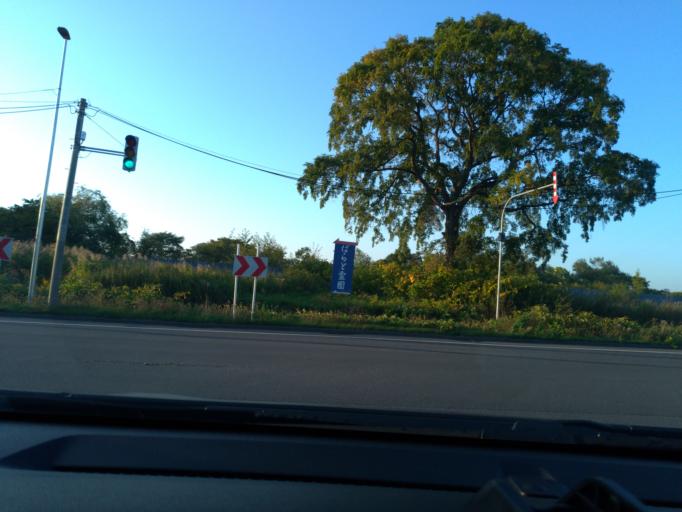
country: JP
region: Hokkaido
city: Ishikari
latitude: 43.1686
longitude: 141.4102
